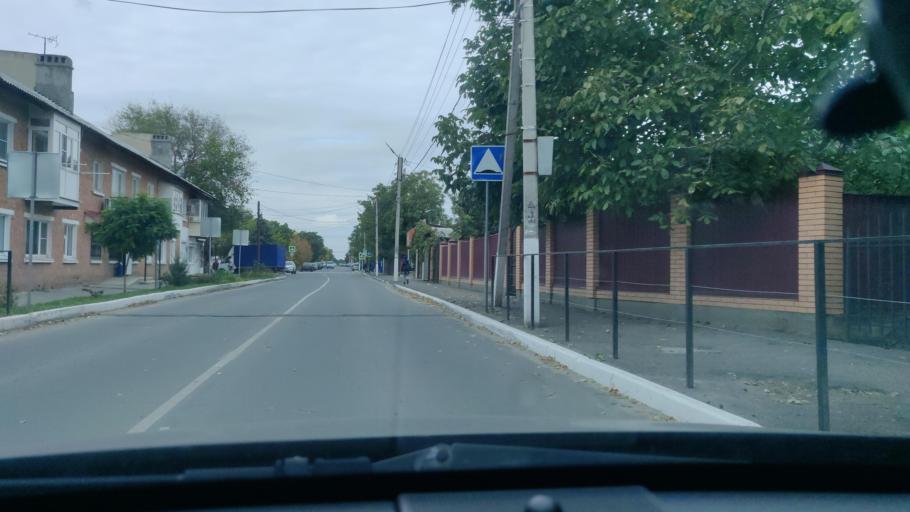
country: RU
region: Rostov
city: Ust'-Donetskiy
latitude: 47.6416
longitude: 40.8692
